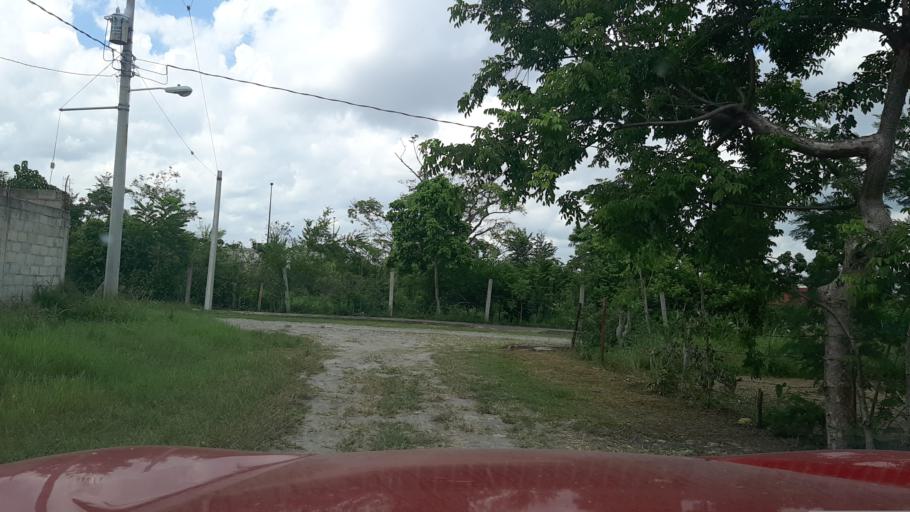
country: MX
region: Veracruz
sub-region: Poza Rica de Hidalgo
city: Villa de las Flores
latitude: 20.5719
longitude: -97.4358
